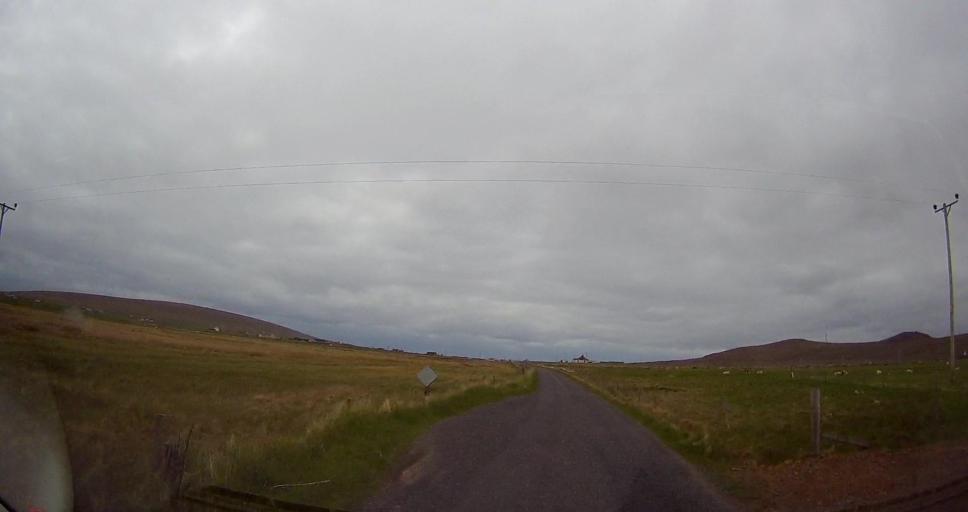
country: GB
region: Scotland
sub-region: Shetland Islands
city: Shetland
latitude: 60.7940
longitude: -0.8530
